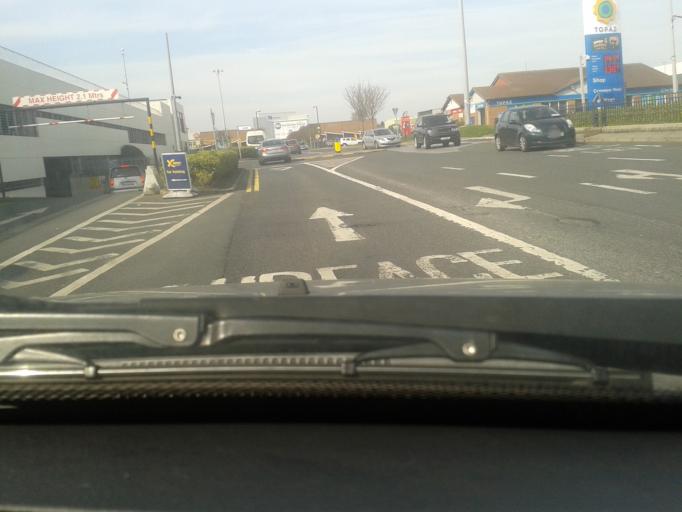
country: IE
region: Leinster
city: Beaumont
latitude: 53.3931
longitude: -6.2467
